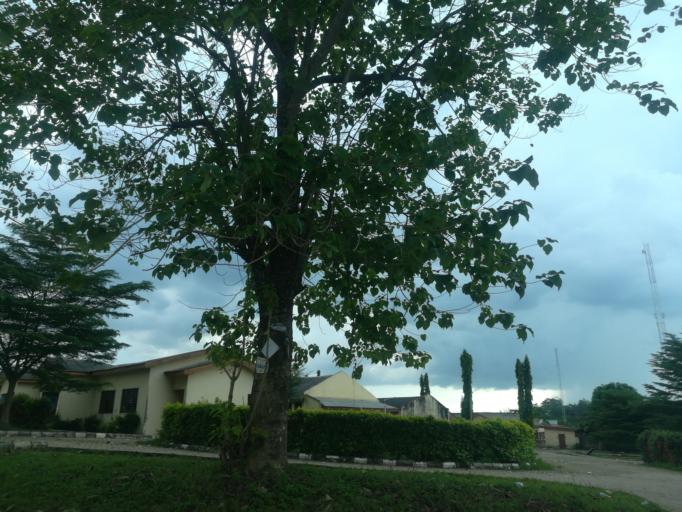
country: NG
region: Oyo
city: Ibadan
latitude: 7.4389
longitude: 3.8830
